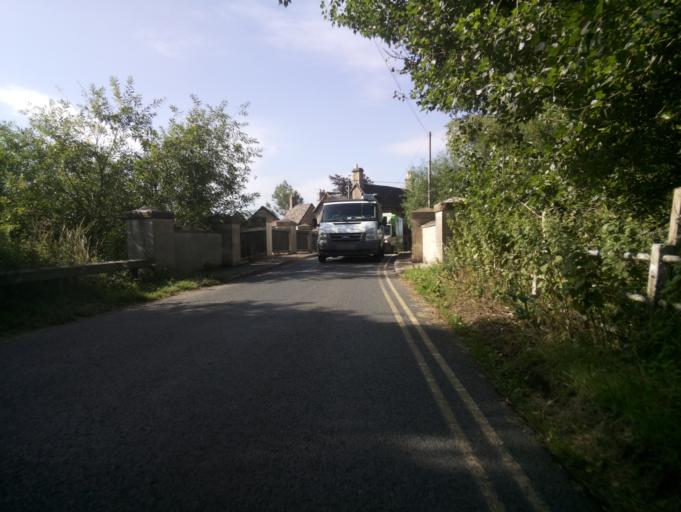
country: GB
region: England
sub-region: Oxfordshire
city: Faringdon
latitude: 51.6945
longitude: -1.5876
